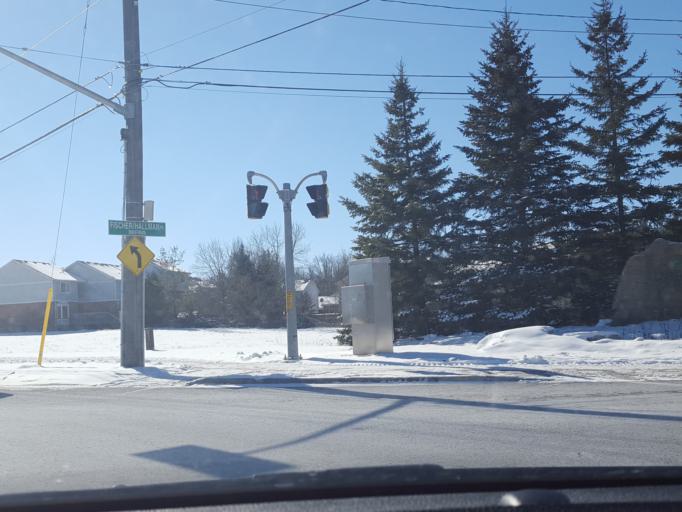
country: CA
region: Ontario
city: Waterloo
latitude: 43.4749
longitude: -80.5722
